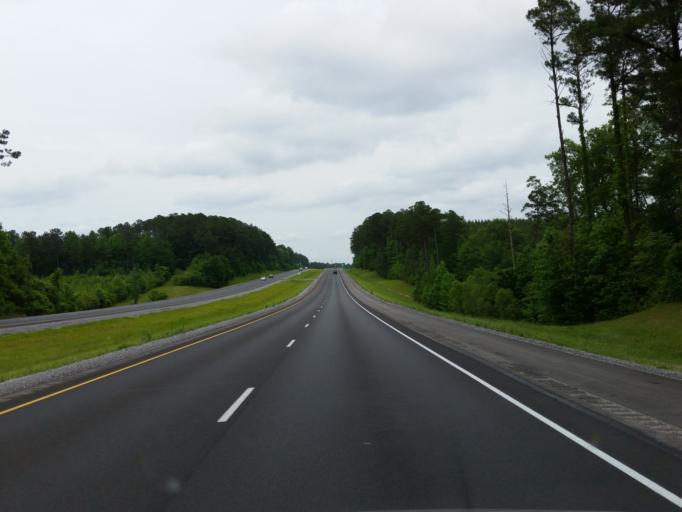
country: US
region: Mississippi
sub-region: Jones County
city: Sharon
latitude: 31.8906
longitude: -89.0337
